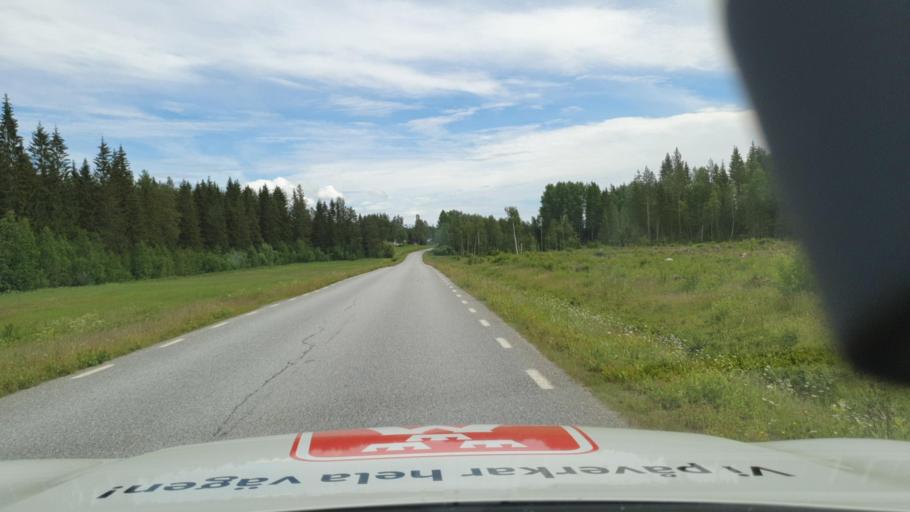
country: SE
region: Vaesterbotten
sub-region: Skelleftea Kommun
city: Soedra Bergsbyn
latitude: 64.5134
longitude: 20.9945
